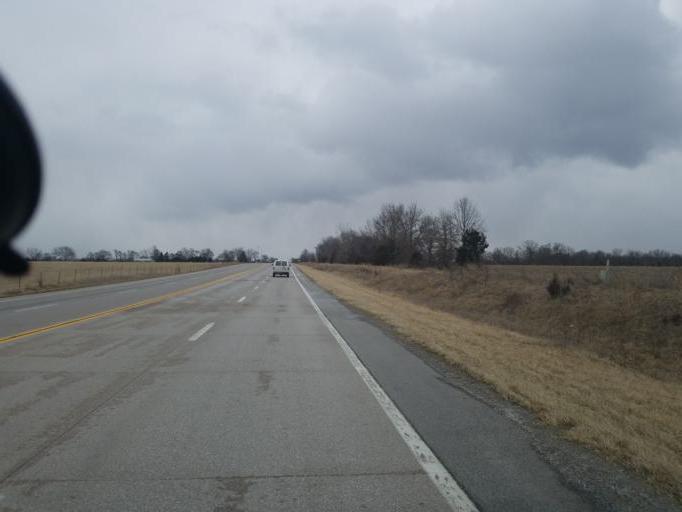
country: US
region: Missouri
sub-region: Macon County
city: Macon
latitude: 39.7807
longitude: -92.4797
